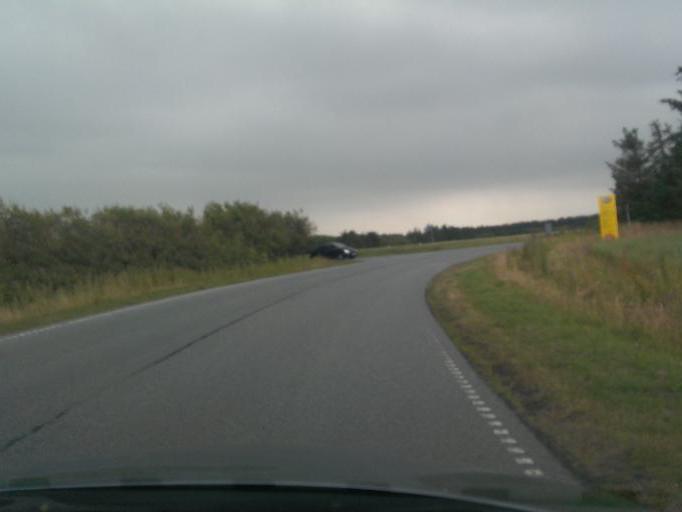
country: DK
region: North Denmark
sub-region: Jammerbugt Kommune
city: Pandrup
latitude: 57.3663
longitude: 9.7300
